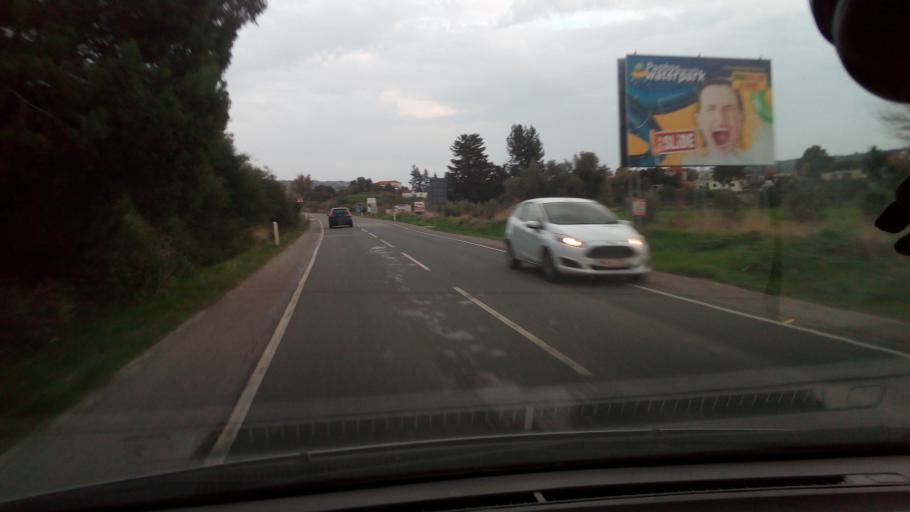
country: CY
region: Pafos
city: Polis
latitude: 35.0070
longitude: 32.4391
